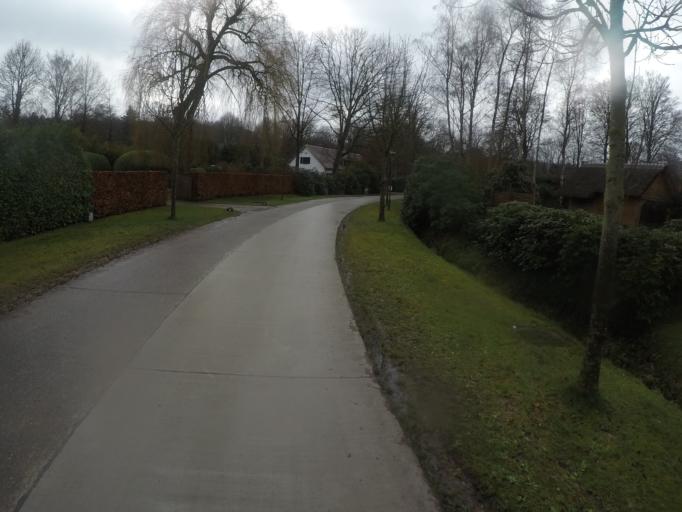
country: BE
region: Flanders
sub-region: Provincie Antwerpen
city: Schilde
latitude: 51.2283
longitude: 4.5634
